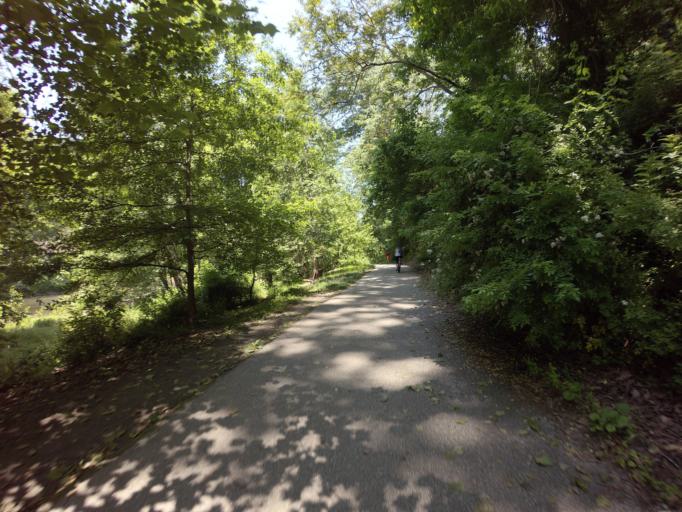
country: US
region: Maryland
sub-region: Howard County
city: Ilchester
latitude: 39.2421
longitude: -76.7499
